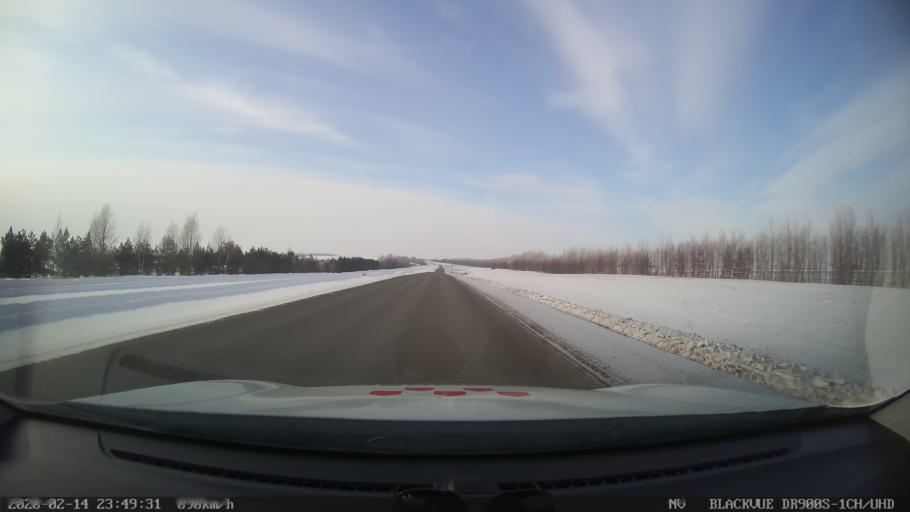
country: RU
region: Tatarstan
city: Kuybyshevskiy Zaton
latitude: 55.2543
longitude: 49.1801
